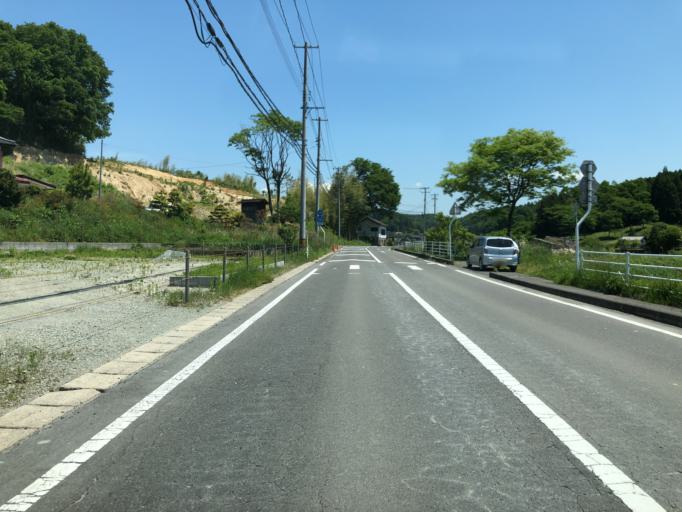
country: JP
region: Fukushima
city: Miharu
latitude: 37.5003
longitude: 140.4703
